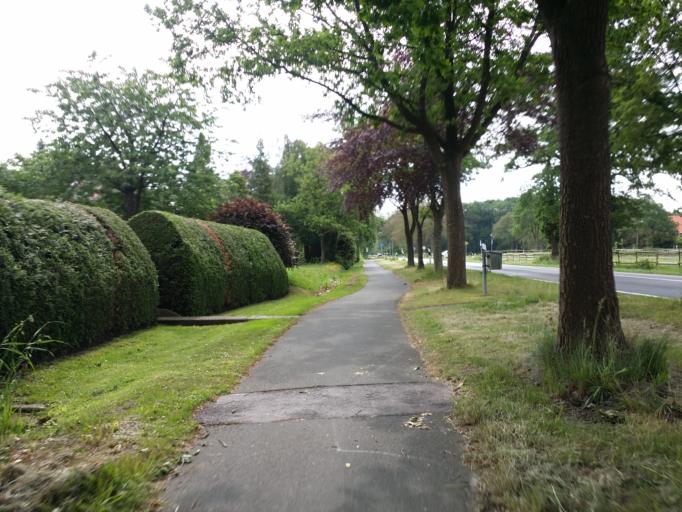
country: DE
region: Lower Saxony
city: Wittmund
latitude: 53.5179
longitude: 7.7921
